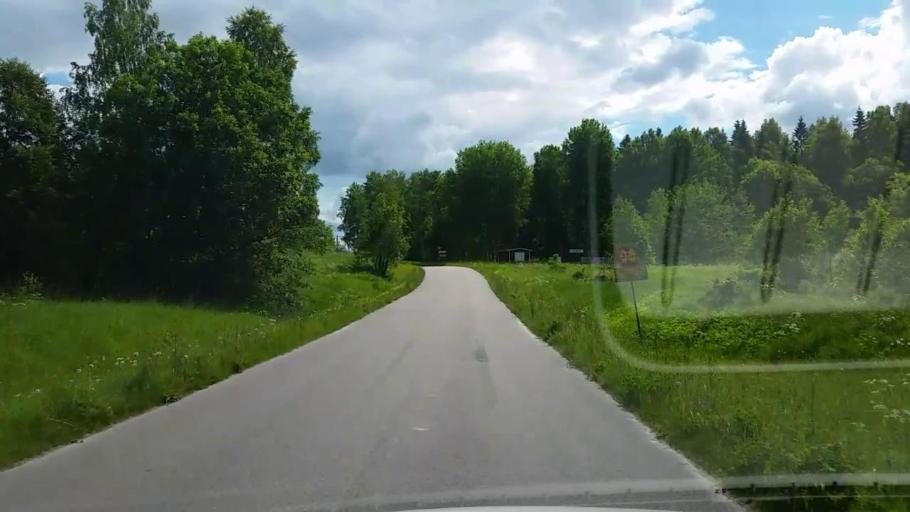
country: SE
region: Vaestmanland
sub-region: Fagersta Kommun
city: Fagersta
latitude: 60.0064
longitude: 15.7675
